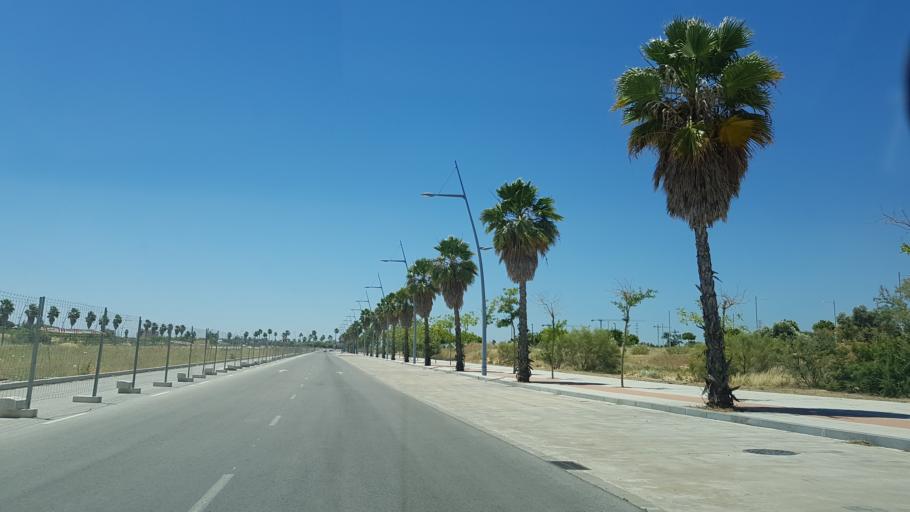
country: ES
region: Andalusia
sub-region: Provincia de Sevilla
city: Dos Hermanas
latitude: 37.3180
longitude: -5.9292
